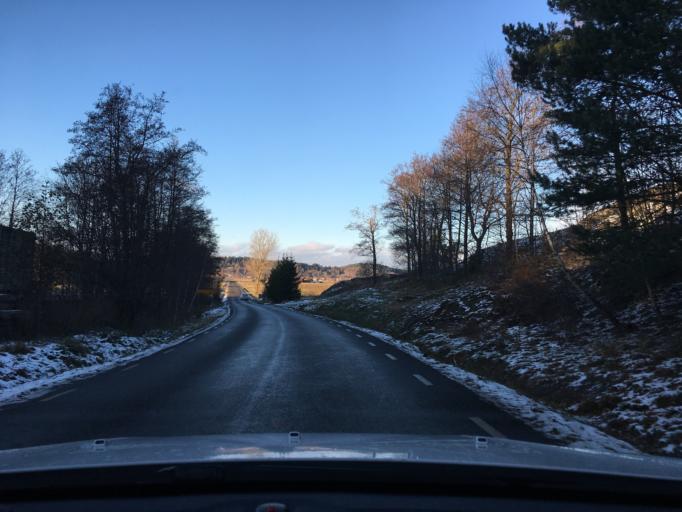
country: SE
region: Vaestra Goetaland
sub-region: Tjorns Kommun
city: Myggenas
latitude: 58.0403
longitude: 11.7334
